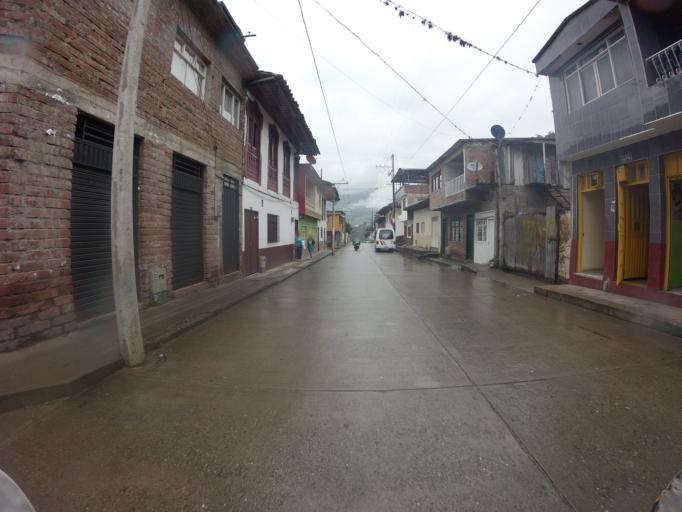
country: CO
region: Quindio
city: Genova
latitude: 4.2066
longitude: -75.7898
